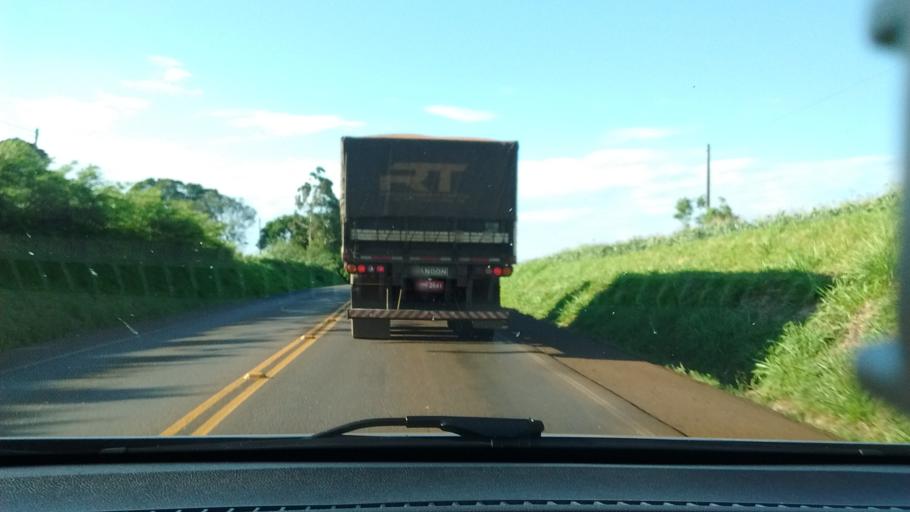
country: BR
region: Parana
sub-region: Cascavel
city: Cascavel
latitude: -25.2345
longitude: -53.5897
